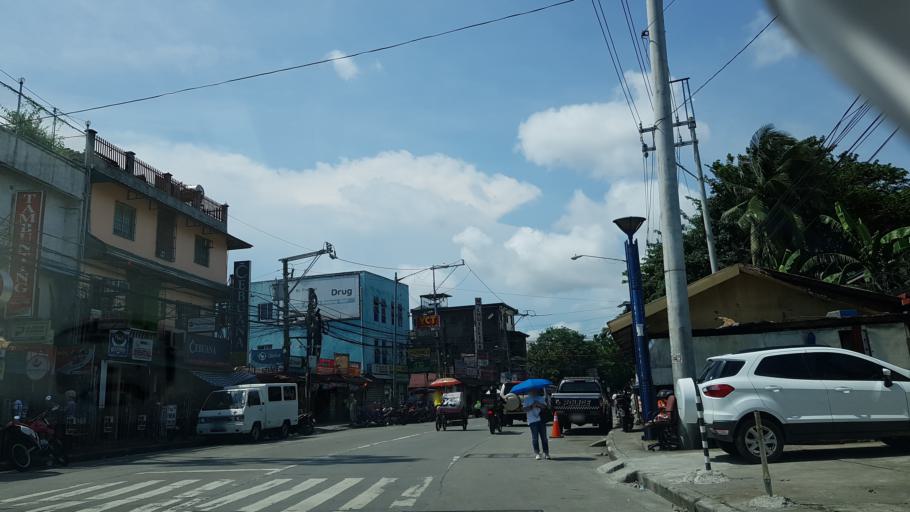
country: PH
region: Metro Manila
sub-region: Makati City
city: Makati City
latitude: 14.5266
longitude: 121.0266
